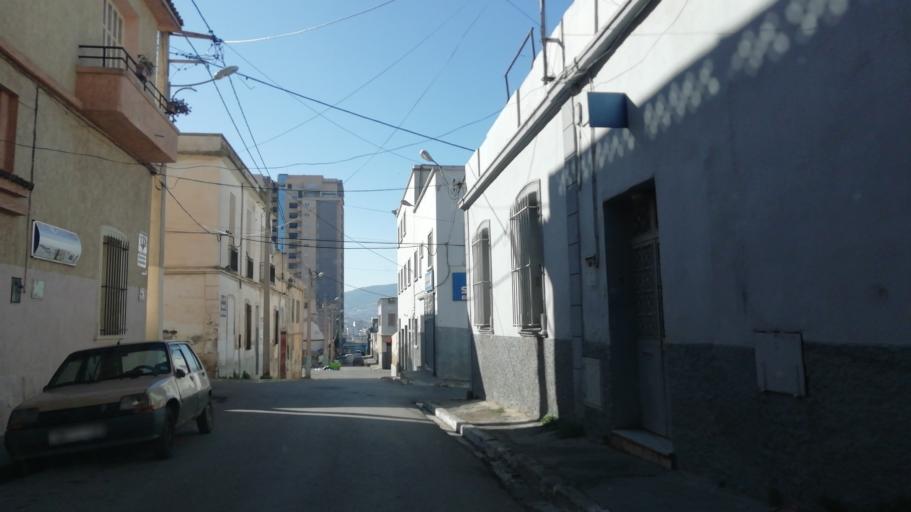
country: DZ
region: Oran
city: Oran
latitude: 35.7059
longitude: -0.6194
